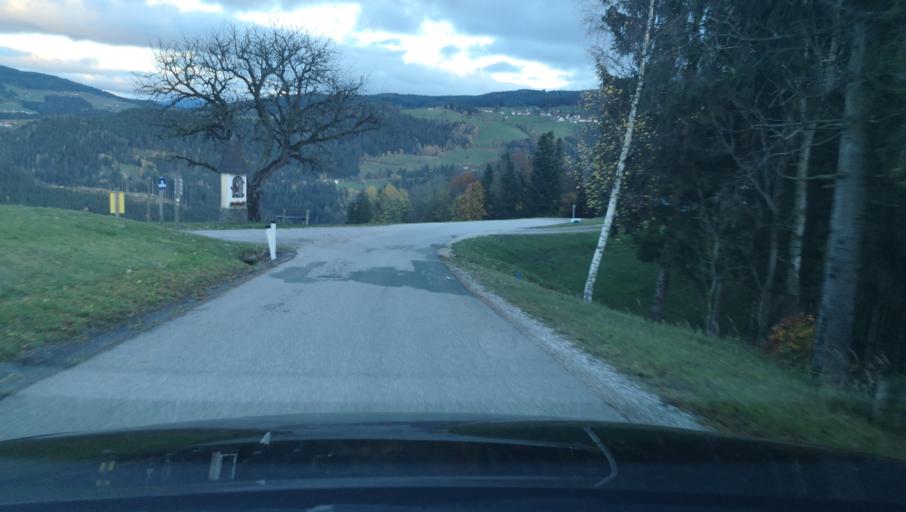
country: AT
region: Styria
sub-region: Politischer Bezirk Weiz
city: Koglhof
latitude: 47.3319
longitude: 15.6773
